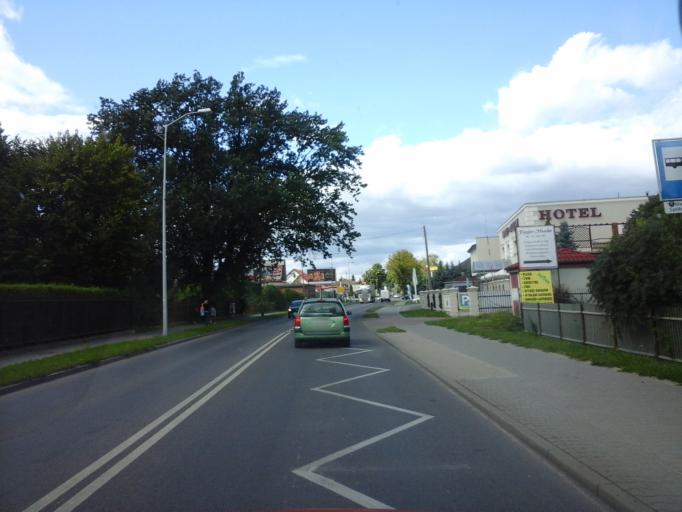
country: PL
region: West Pomeranian Voivodeship
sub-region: Powiat policki
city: Przeclaw
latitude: 53.4277
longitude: 14.4755
